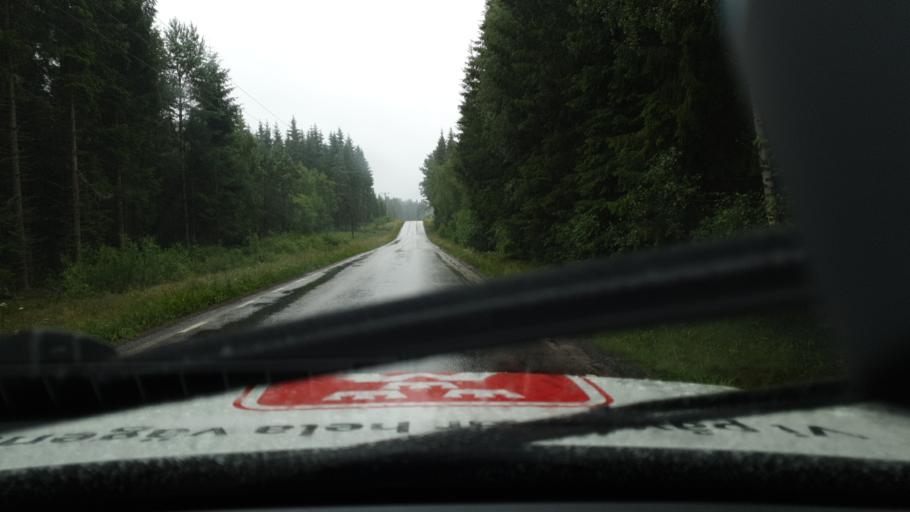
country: SE
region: Vaestra Goetaland
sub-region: Falkopings Kommun
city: Floby
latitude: 58.1774
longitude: 13.3456
